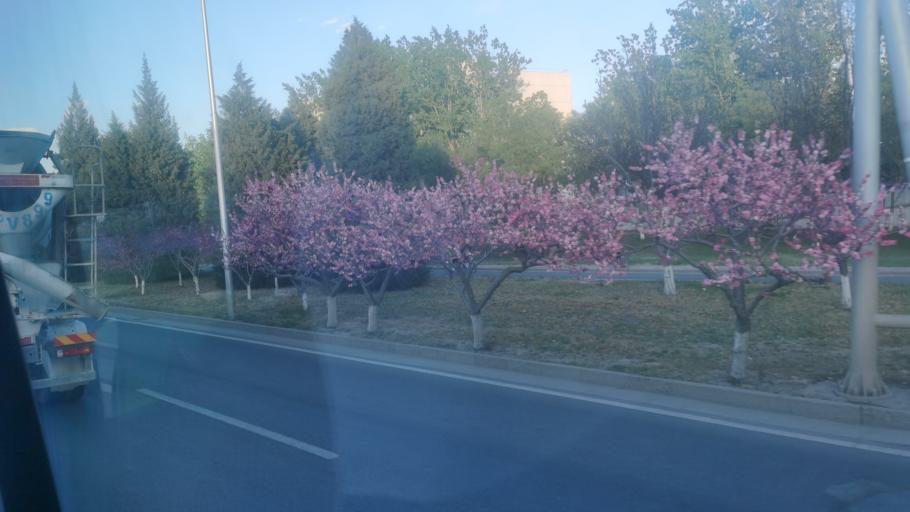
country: CN
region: Beijing
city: Xibeiwang
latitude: 40.0787
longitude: 116.2566
